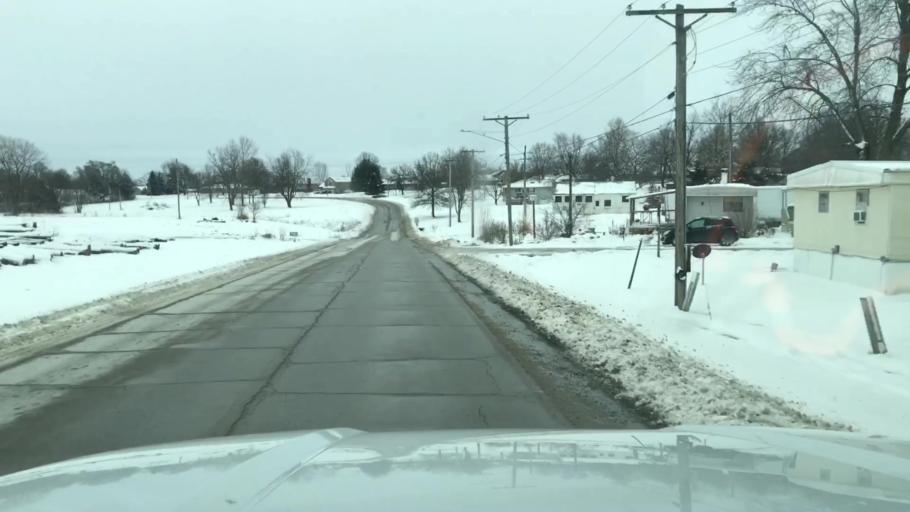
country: US
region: Missouri
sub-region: Clinton County
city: Cameron
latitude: 39.7445
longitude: -94.2280
